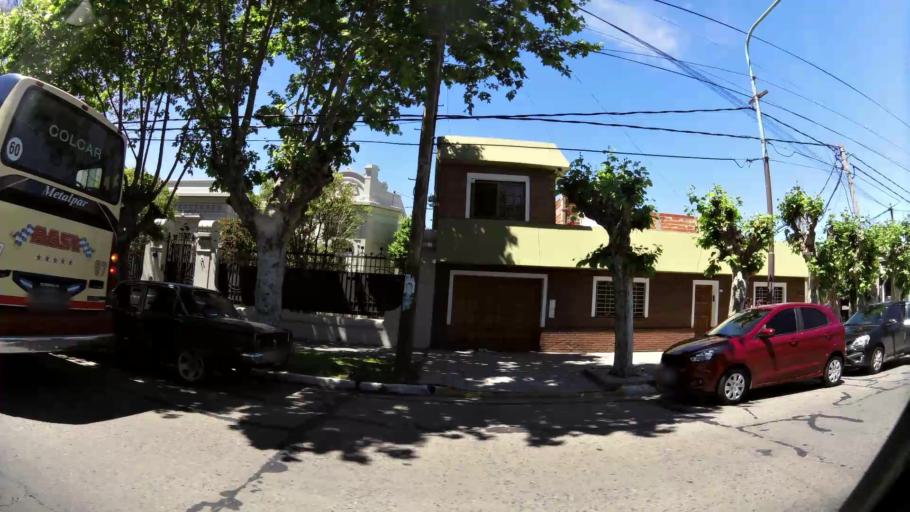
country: AR
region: Buenos Aires
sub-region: Partido de Quilmes
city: Quilmes
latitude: -34.7124
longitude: -58.2760
